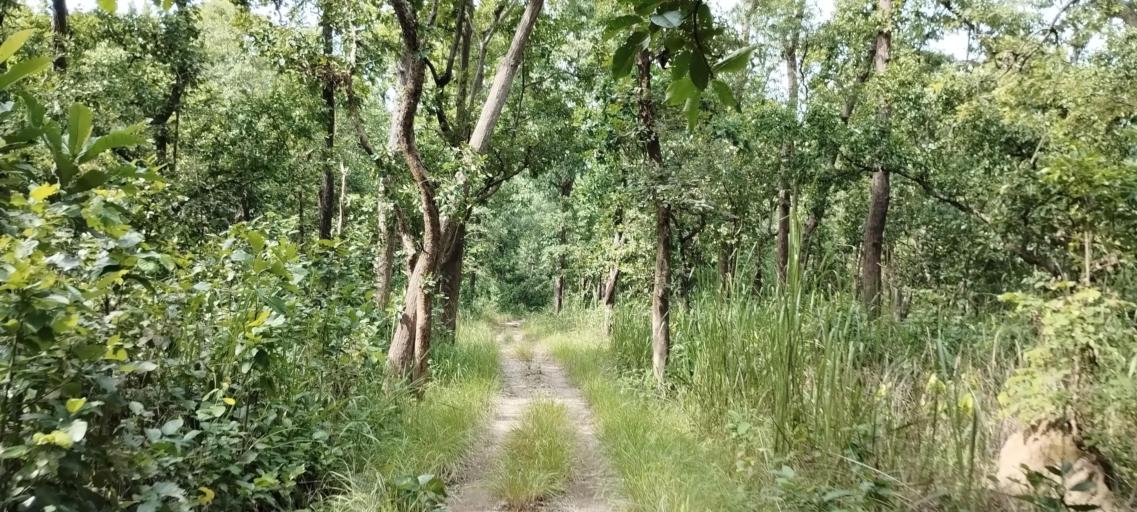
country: NP
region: Far Western
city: Tikapur
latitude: 28.5328
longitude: 81.2832
